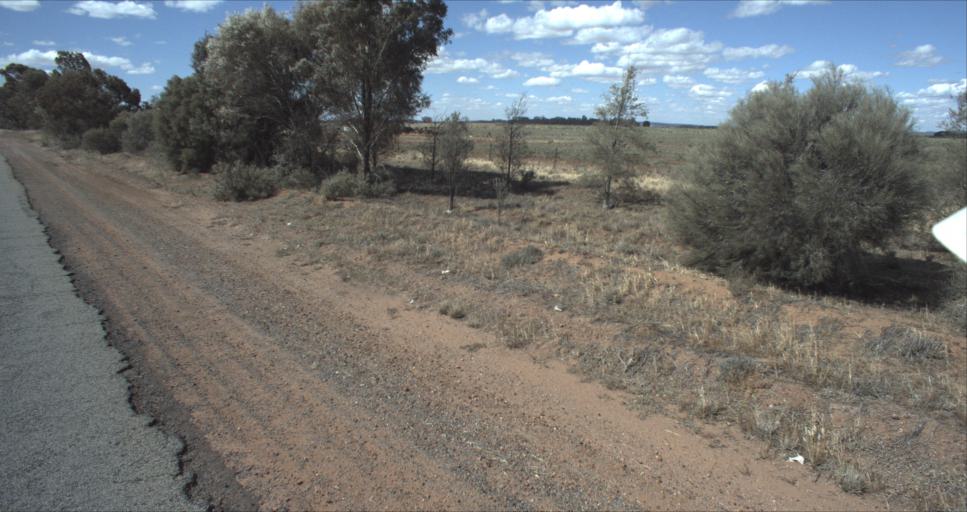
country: AU
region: New South Wales
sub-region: Leeton
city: Leeton
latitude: -34.4762
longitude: 146.2500
